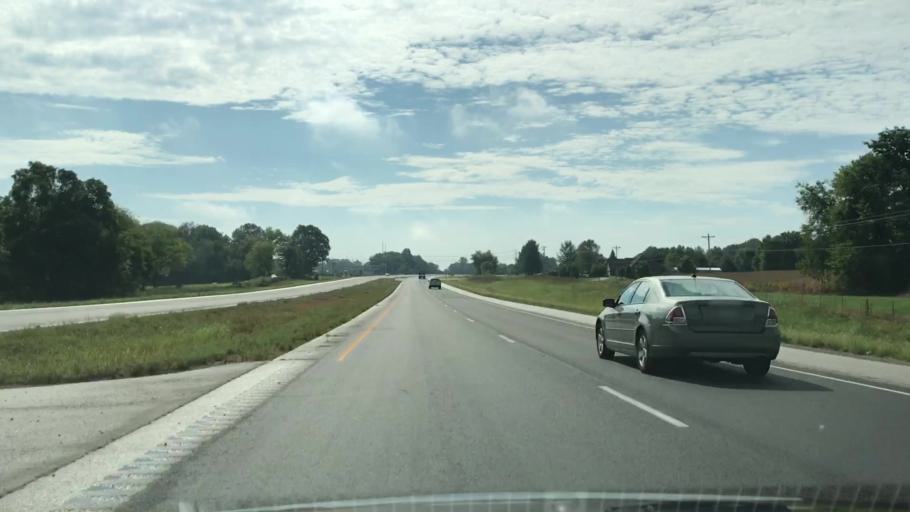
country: US
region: Kentucky
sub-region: Warren County
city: Plano
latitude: 36.8832
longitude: -86.3628
